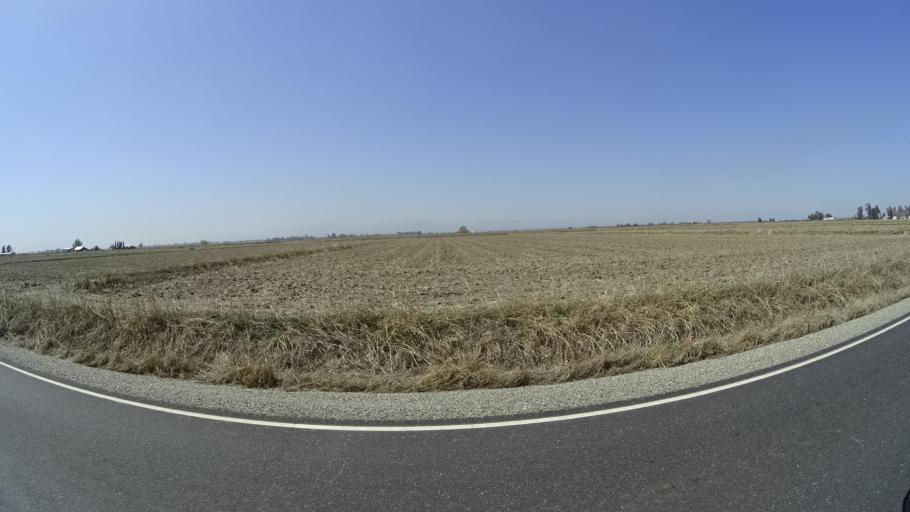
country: US
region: California
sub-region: Glenn County
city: Willows
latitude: 39.5469
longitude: -122.1366
